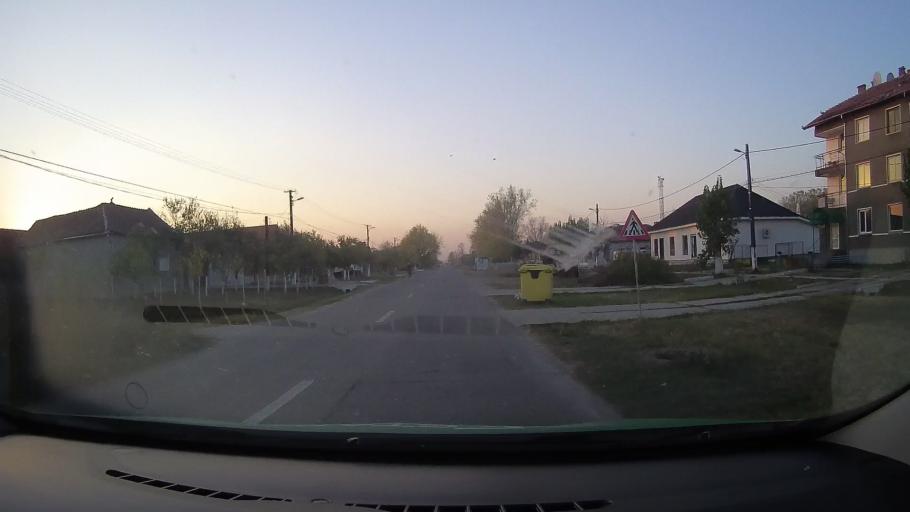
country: RO
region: Arad
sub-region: Comuna Zarand
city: Zarand
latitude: 46.4031
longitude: 21.6458
